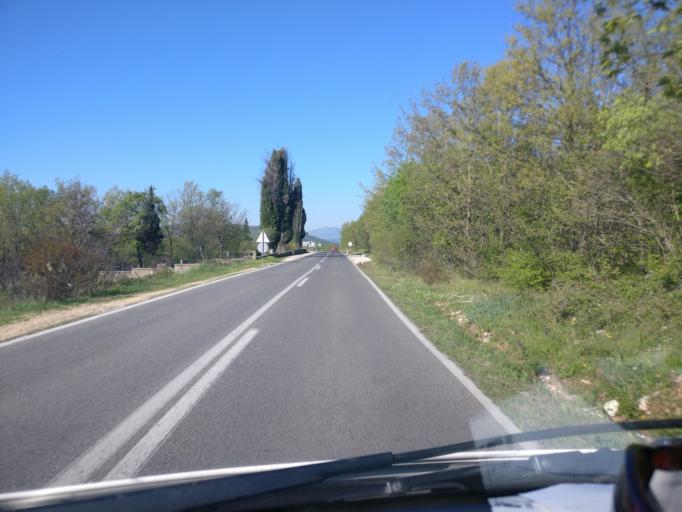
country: BA
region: Federation of Bosnia and Herzegovina
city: Tasovcici
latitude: 43.1319
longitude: 17.7705
